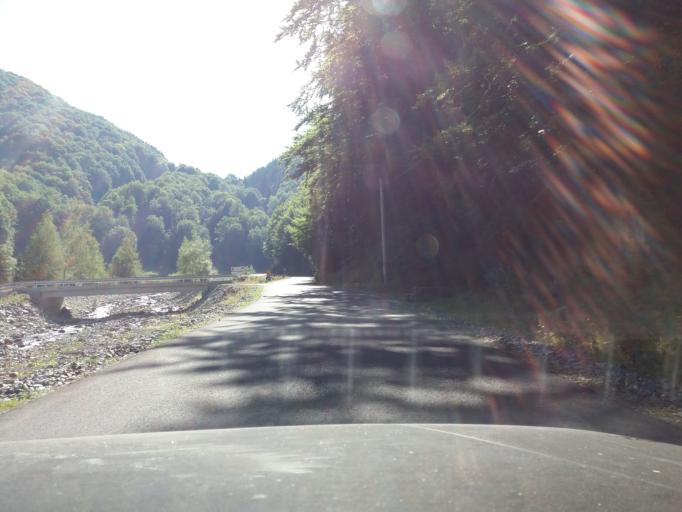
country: RO
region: Hunedoara
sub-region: Oras Petrila
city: Petrila
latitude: 45.4169
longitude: 23.4582
